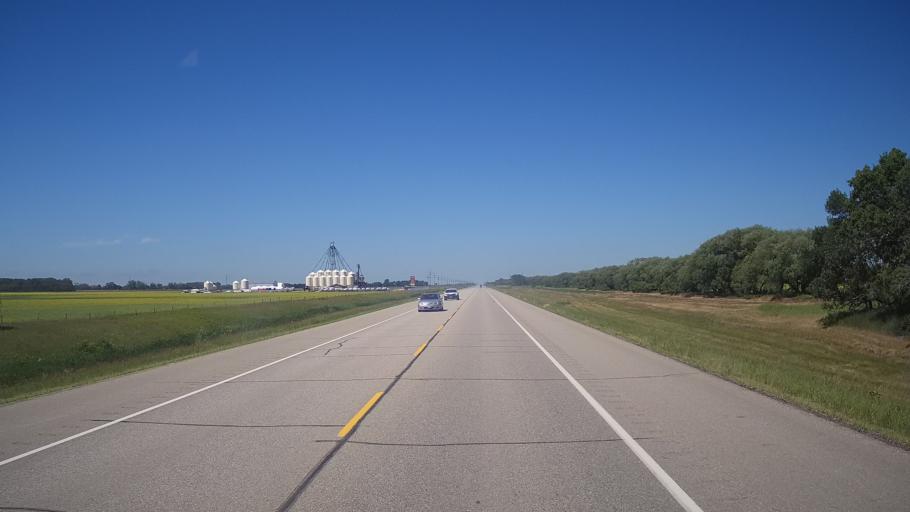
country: CA
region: Manitoba
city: Neepawa
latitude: 50.2257
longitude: -99.0337
